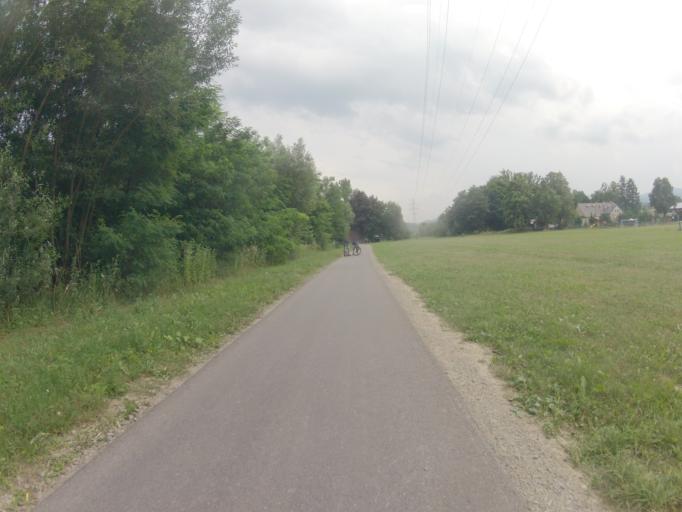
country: PL
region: Lesser Poland Voivodeship
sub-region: Powiat nowosadecki
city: Stary Sacz
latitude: 49.5415
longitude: 20.6563
